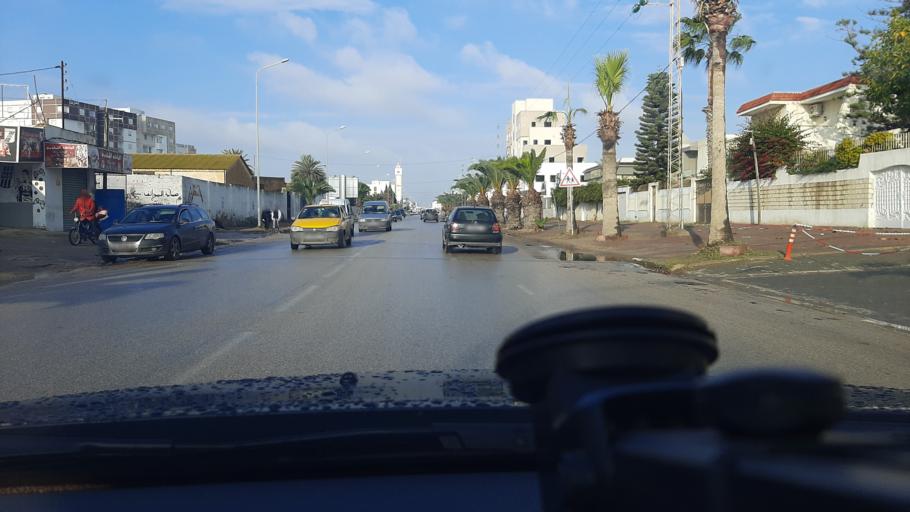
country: TN
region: Safaqis
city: Sfax
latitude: 34.7433
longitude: 10.7323
